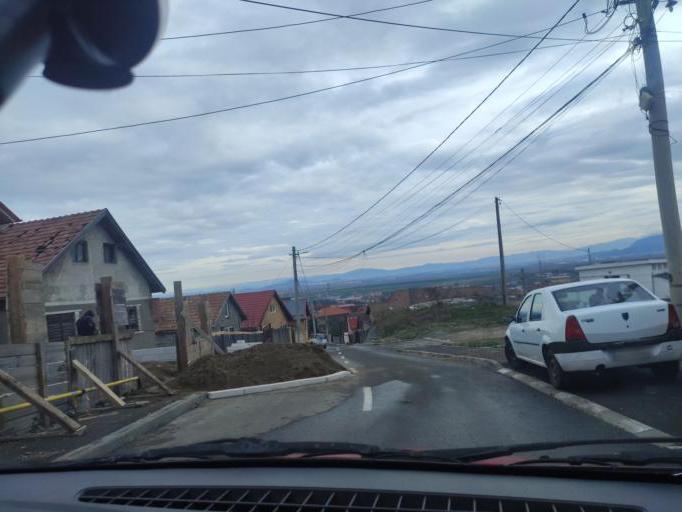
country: RO
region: Brasov
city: Codlea
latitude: 45.6941
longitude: 25.4351
